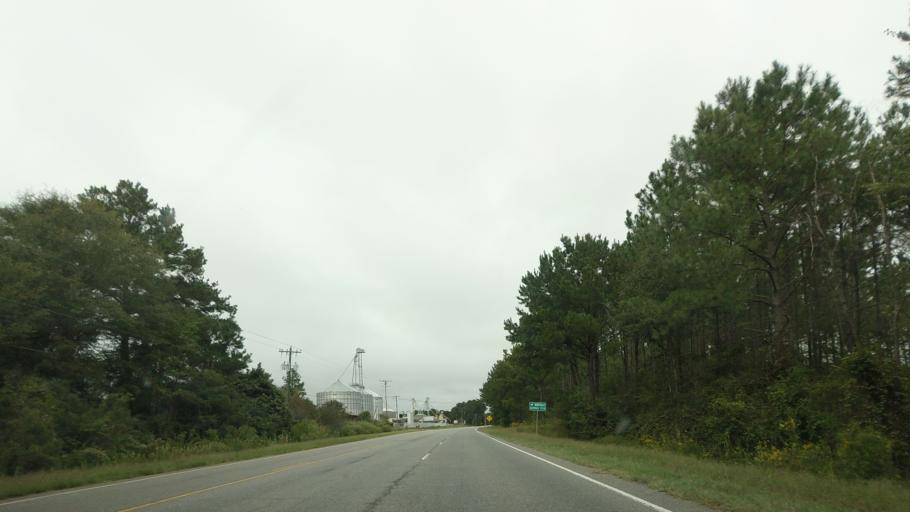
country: US
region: Georgia
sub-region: Irwin County
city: Ocilla
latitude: 31.6438
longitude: -83.2461
